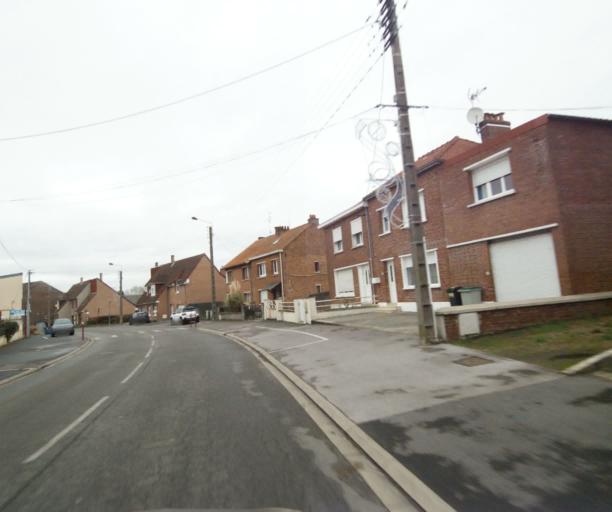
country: FR
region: Nord-Pas-de-Calais
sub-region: Departement du Nord
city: Aubry-du-Hainaut
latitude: 50.3706
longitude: 3.4723
